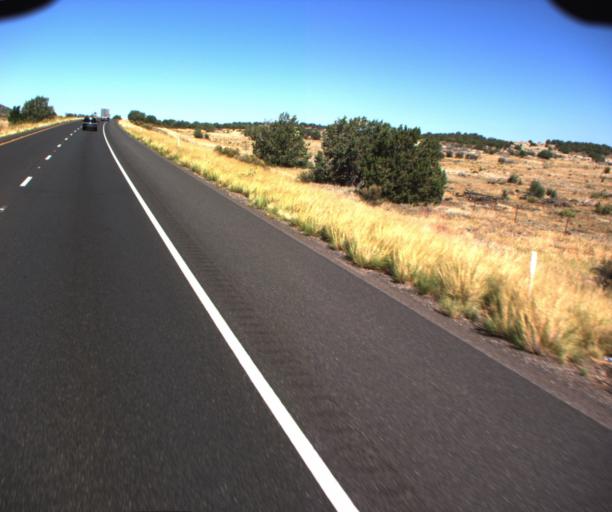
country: US
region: Arizona
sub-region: Yavapai County
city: Paulden
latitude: 35.2582
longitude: -112.7121
